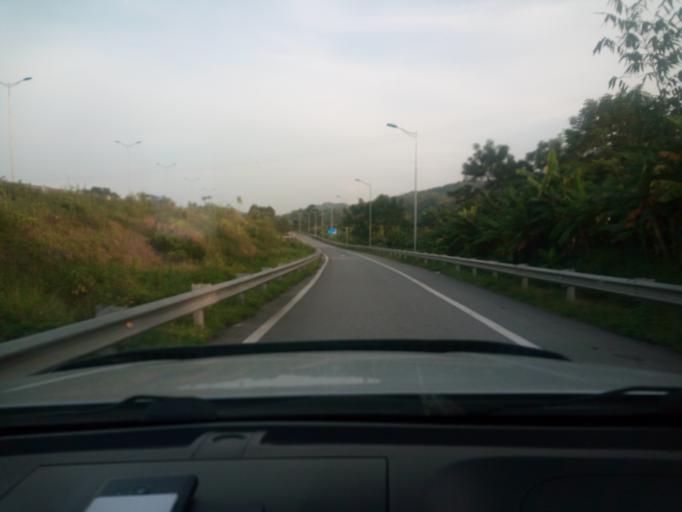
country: VN
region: Yen Bai
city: Co Phuc
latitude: 21.8784
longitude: 104.6731
